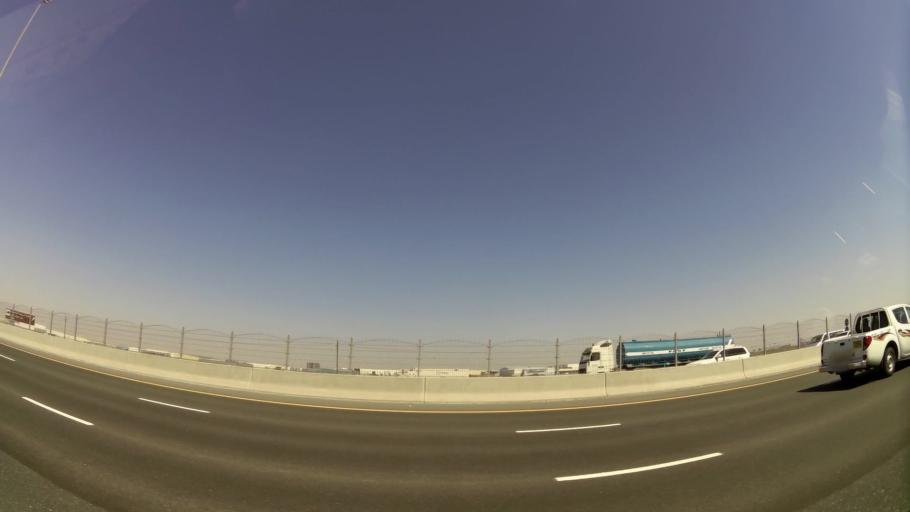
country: AE
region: Dubai
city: Dubai
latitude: 24.9404
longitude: 55.1256
